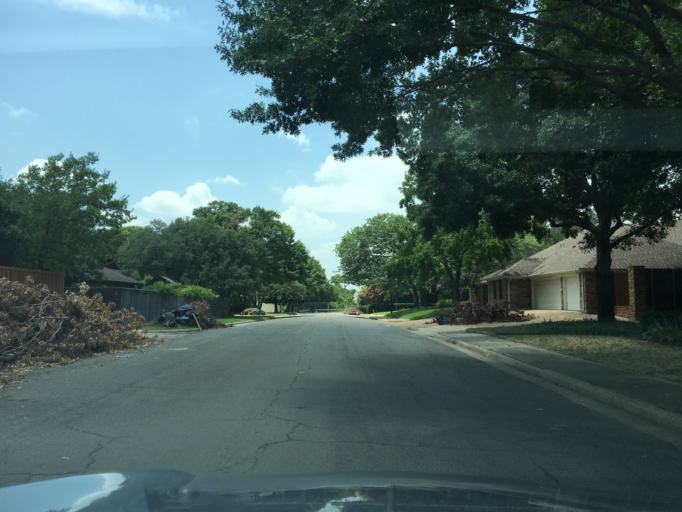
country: US
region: Texas
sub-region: Dallas County
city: Addison
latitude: 32.9153
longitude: -96.7933
